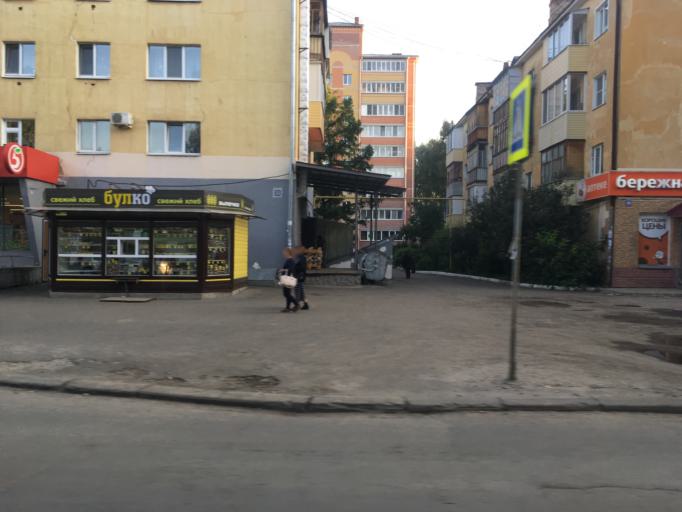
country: RU
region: Mariy-El
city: Yoshkar-Ola
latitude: 56.6473
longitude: 47.8839
